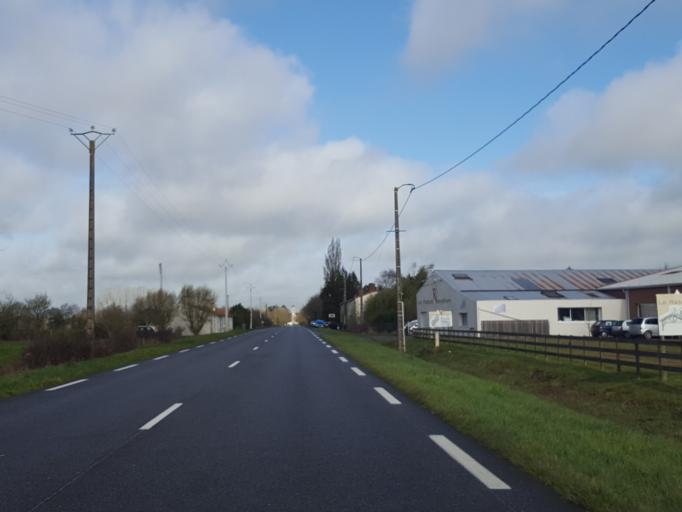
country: FR
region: Pays de la Loire
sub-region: Departement de la Vendee
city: Les Lucs-sur-Boulogne
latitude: 46.8308
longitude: -1.4811
